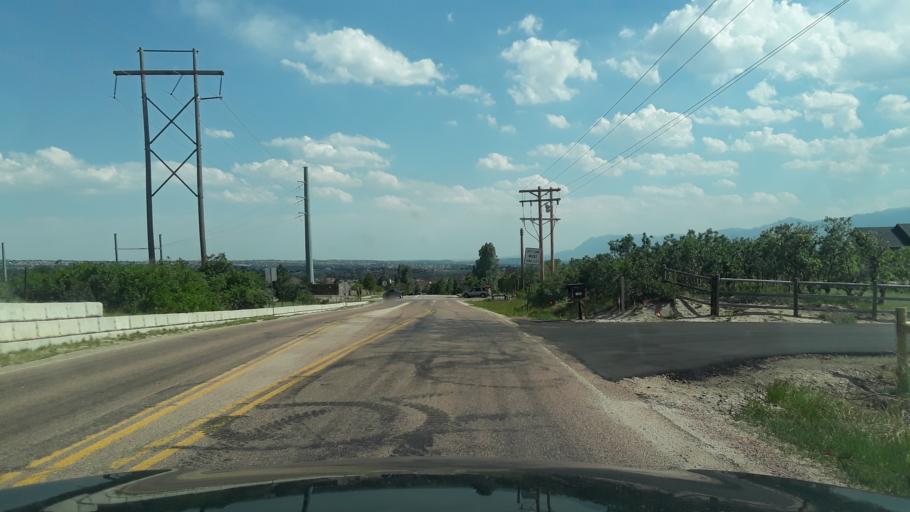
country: US
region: Colorado
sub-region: El Paso County
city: Gleneagle
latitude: 39.0358
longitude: -104.7849
